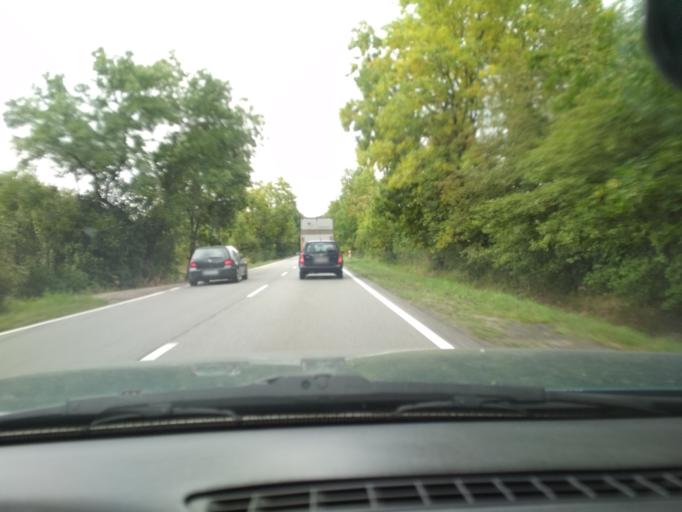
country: PL
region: Silesian Voivodeship
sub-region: Powiat zawiercianski
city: Wysoka
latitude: 50.4373
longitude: 19.3511
